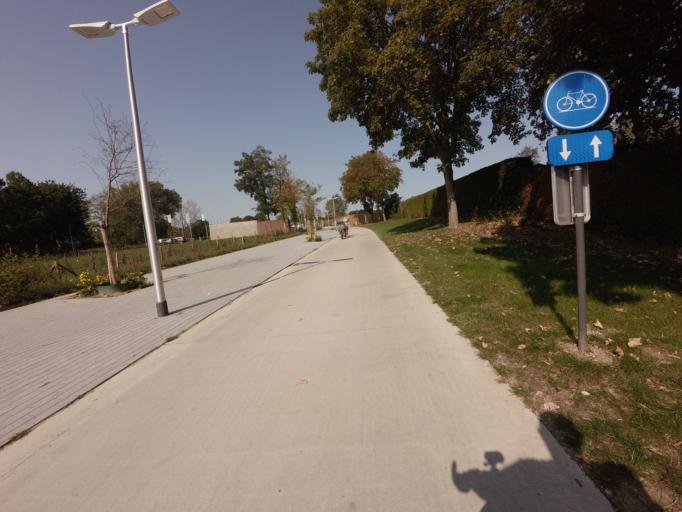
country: BE
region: Flanders
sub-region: Provincie Limburg
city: Maaseik
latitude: 51.1246
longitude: 5.8153
